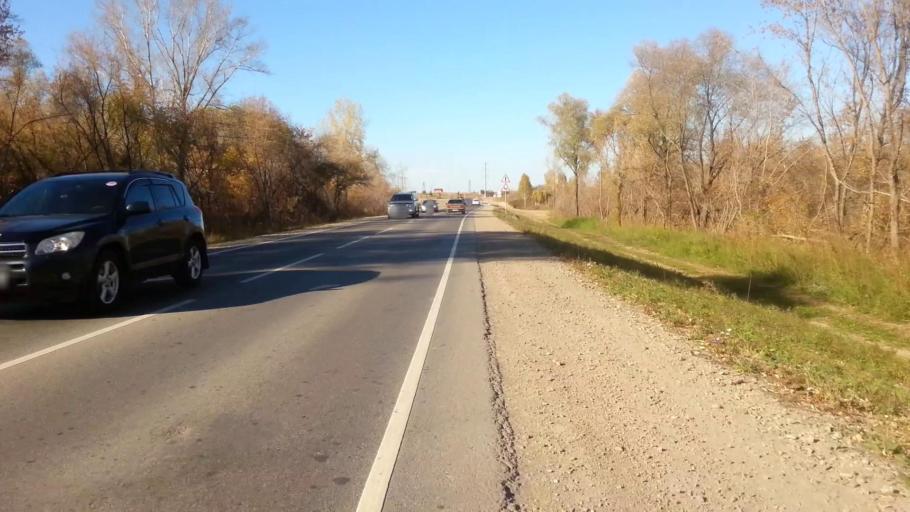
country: RU
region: Altai Krai
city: Sannikovo
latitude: 53.3250
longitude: 83.9424
